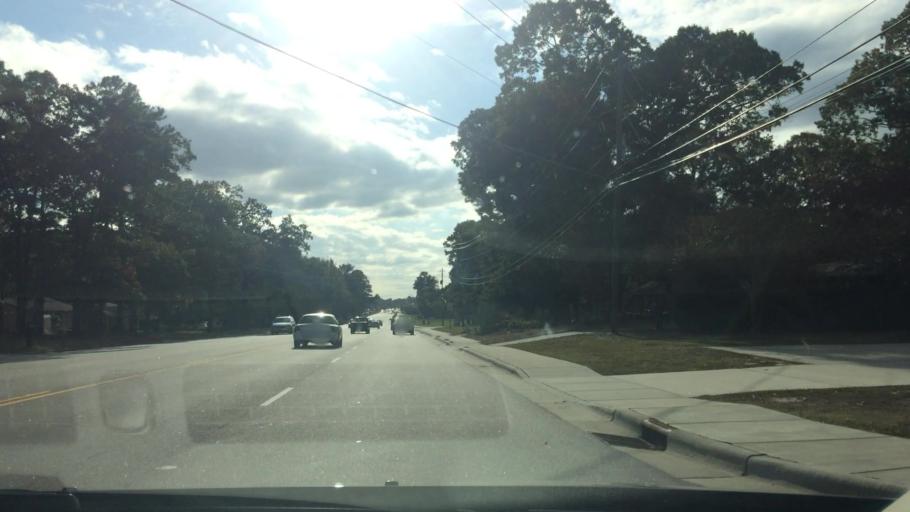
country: US
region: North Carolina
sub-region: Wayne County
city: Elroy
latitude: 35.3872
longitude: -77.9225
